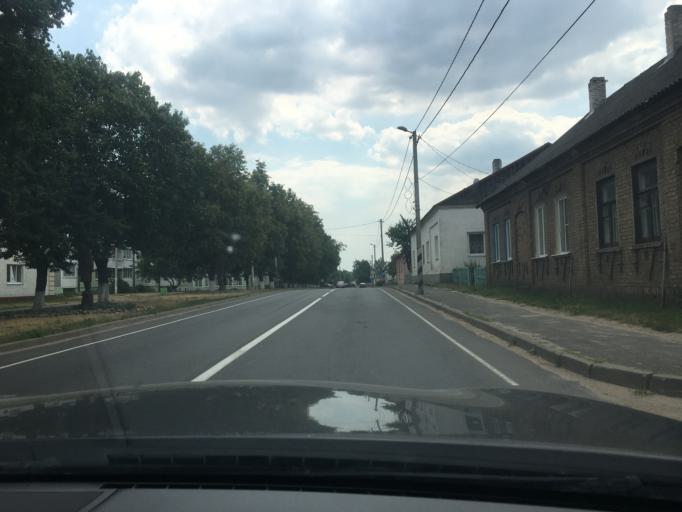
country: BY
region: Brest
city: Ruzhany
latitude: 52.8629
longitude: 24.8909
